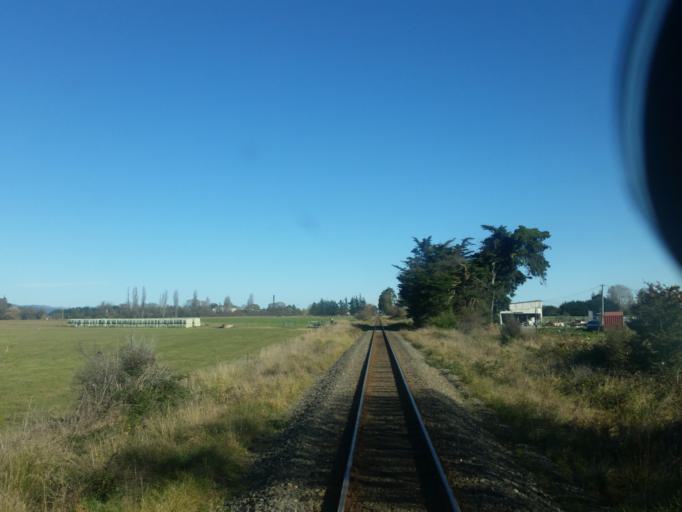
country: NZ
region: Canterbury
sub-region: Waimakariri District
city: Kaiapoi
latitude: -43.4367
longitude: 172.6474
